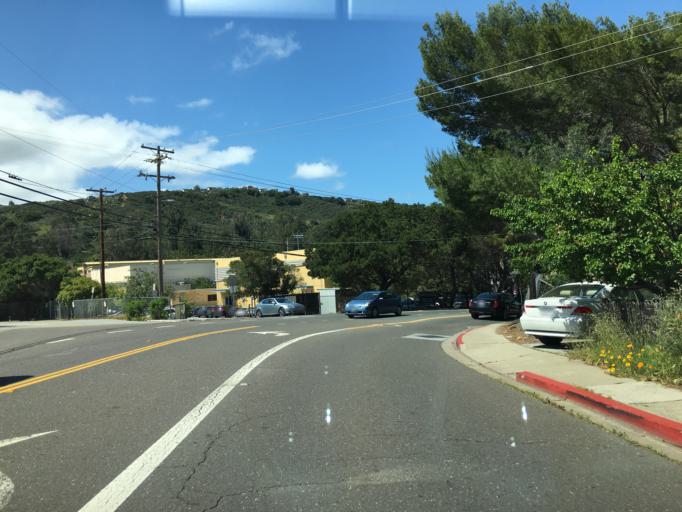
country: US
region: California
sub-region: San Mateo County
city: Belmont
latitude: 37.5068
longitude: -122.2861
